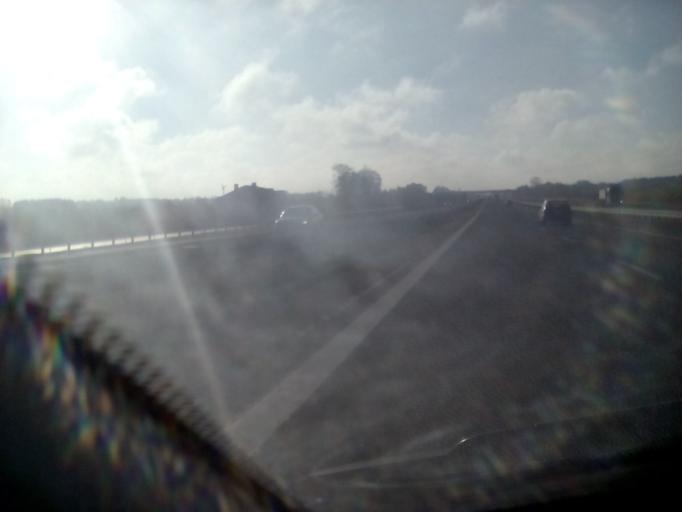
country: PL
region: Masovian Voivodeship
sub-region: Powiat grojecki
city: Jasieniec
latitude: 51.8053
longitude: 20.8874
